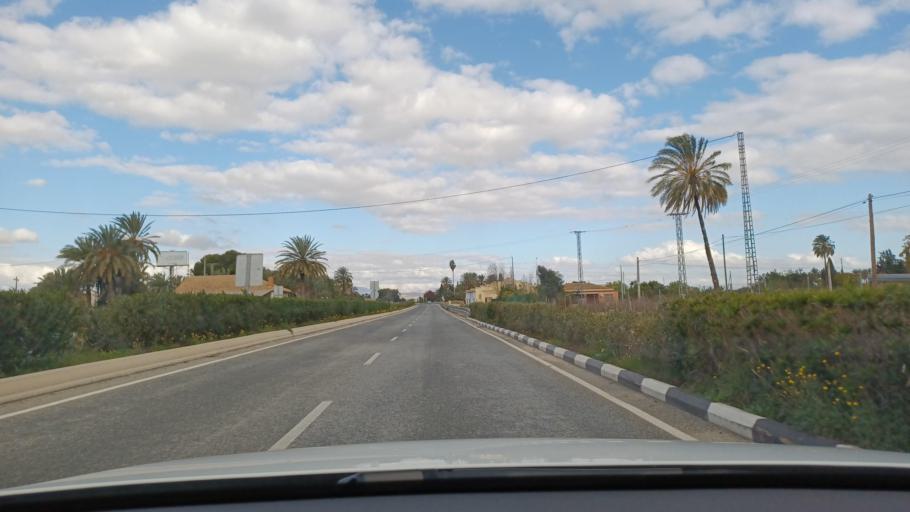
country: ES
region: Valencia
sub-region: Provincia de Alicante
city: Elche
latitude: 38.1961
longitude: -0.7005
